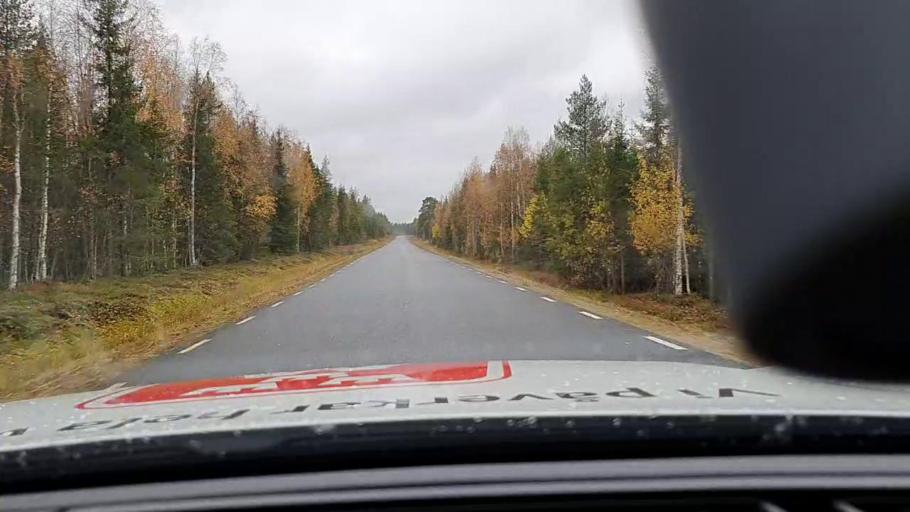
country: SE
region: Norrbotten
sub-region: Haparanda Kommun
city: Haparanda
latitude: 65.9345
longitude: 23.8131
